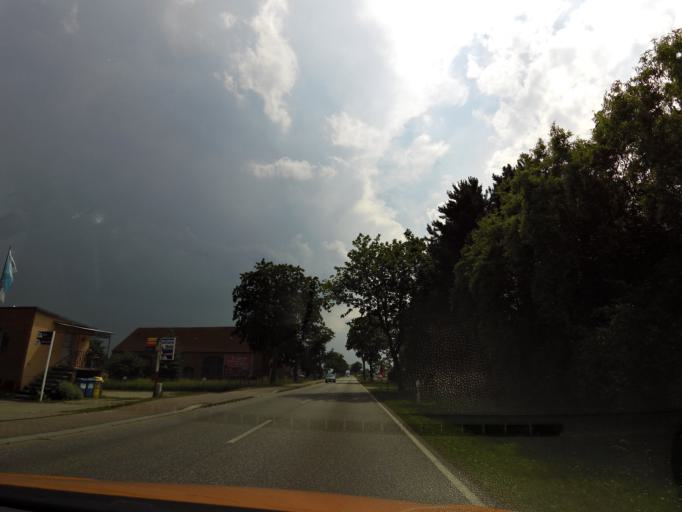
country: DE
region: Brandenburg
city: Kyritz
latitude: 52.9381
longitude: 12.4073
